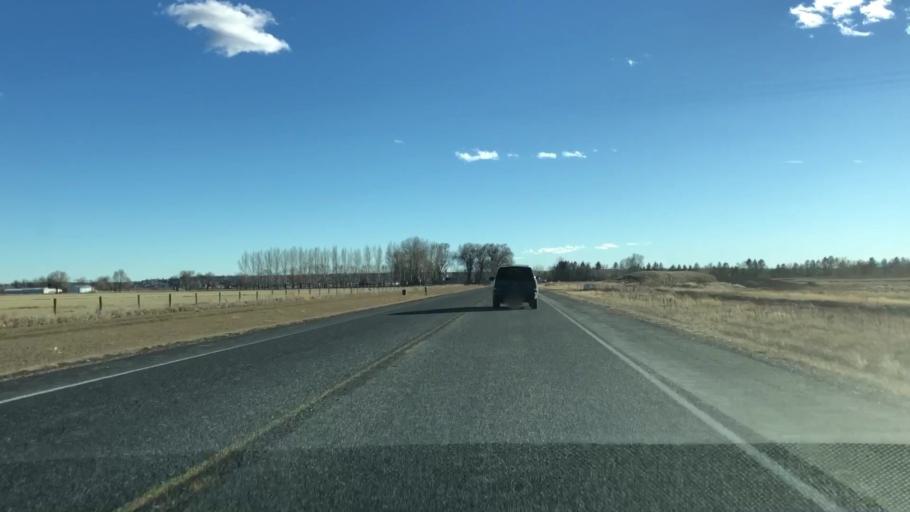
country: US
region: Colorado
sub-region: Weld County
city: Windsor
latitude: 40.5123
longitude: -104.9818
